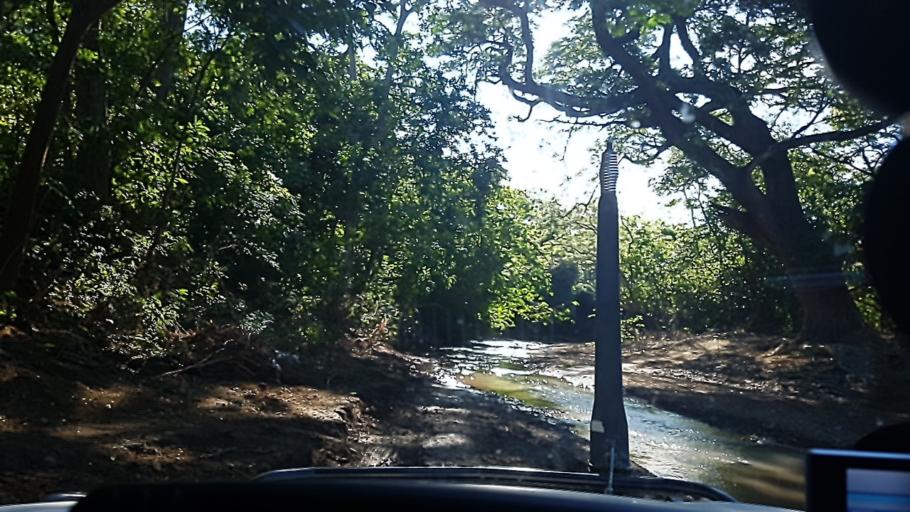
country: NI
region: Rivas
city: Tola
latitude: 11.5417
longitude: -86.1134
